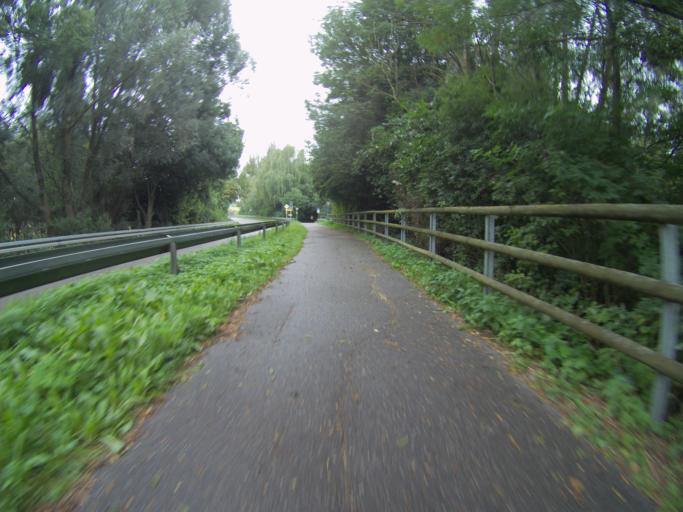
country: DE
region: Bavaria
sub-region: Upper Bavaria
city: Marzling
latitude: 48.3892
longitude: 11.7921
